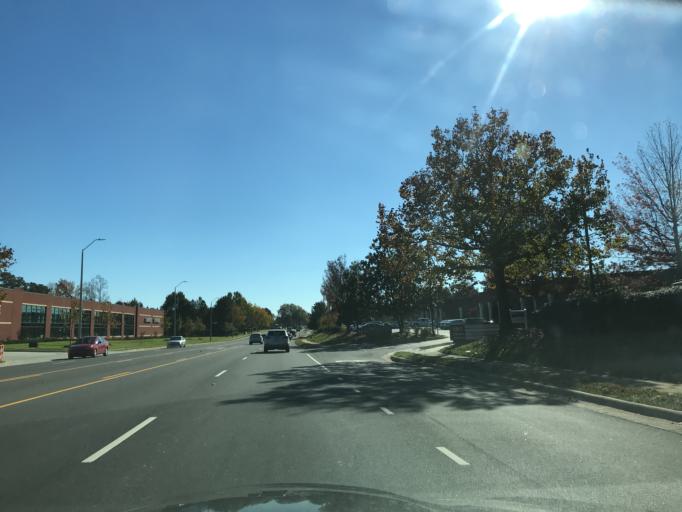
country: US
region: North Carolina
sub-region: Wake County
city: Raleigh
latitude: 35.8449
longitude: -78.6016
